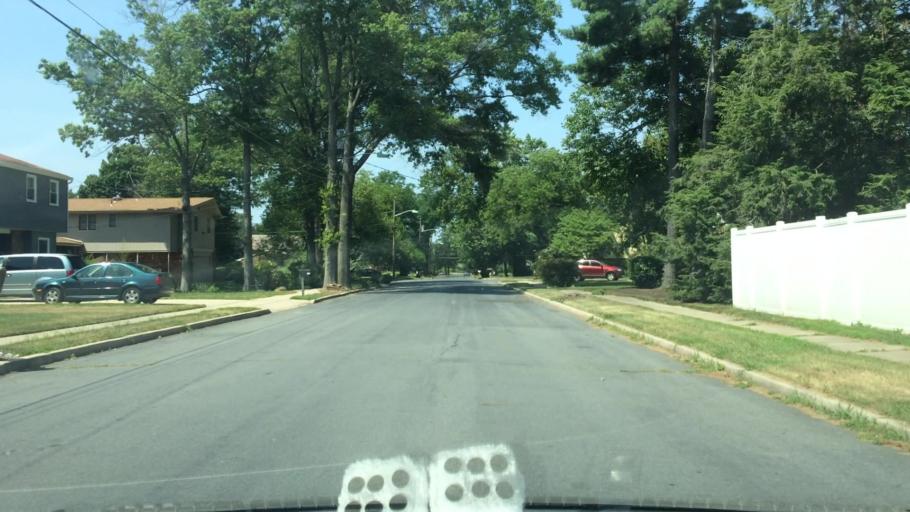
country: US
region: New Jersey
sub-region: Camden County
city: Cherry Hill Mall
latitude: 39.9364
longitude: -75.0053
